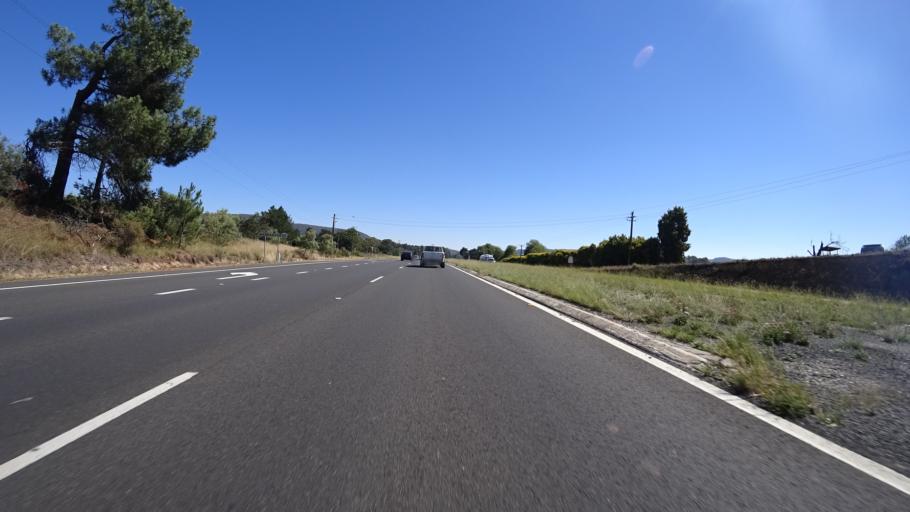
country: AU
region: New South Wales
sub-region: Lithgow
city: Lithgow
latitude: -33.4593
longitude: 150.1203
